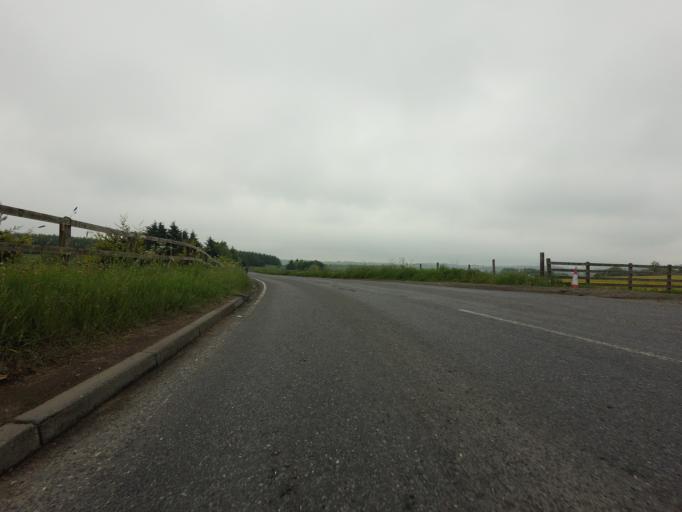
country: GB
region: Scotland
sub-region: Fife
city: Townhill
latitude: 56.1223
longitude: -3.4393
